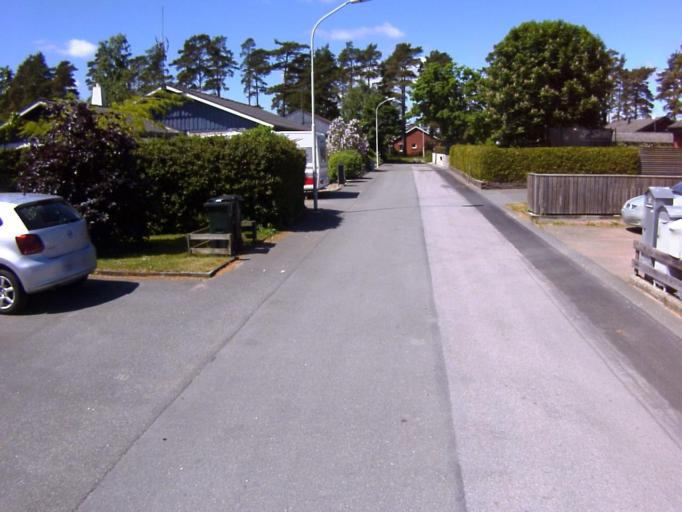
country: SE
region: Skane
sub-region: Kristianstads Kommun
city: Ahus
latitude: 55.9437
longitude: 14.2826
